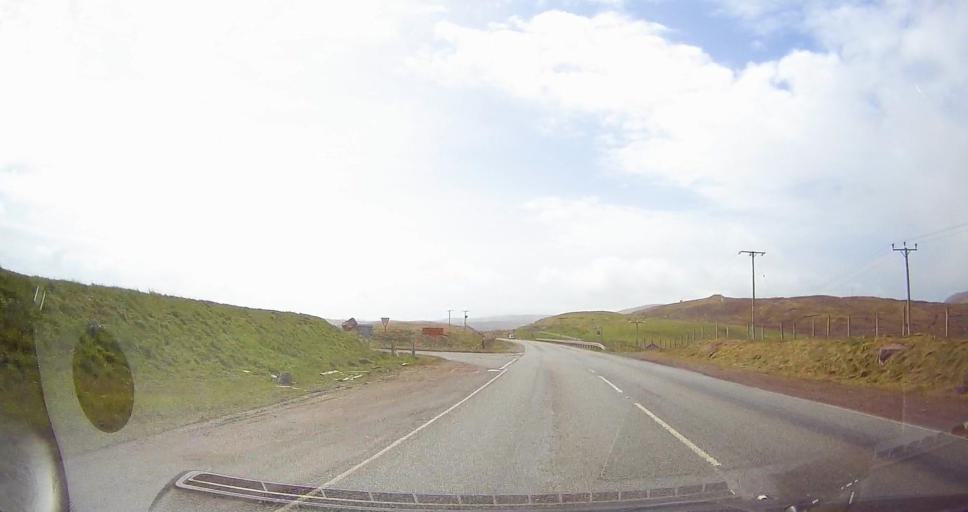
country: GB
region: Scotland
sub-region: Shetland Islands
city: Lerwick
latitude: 60.1155
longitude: -1.2178
